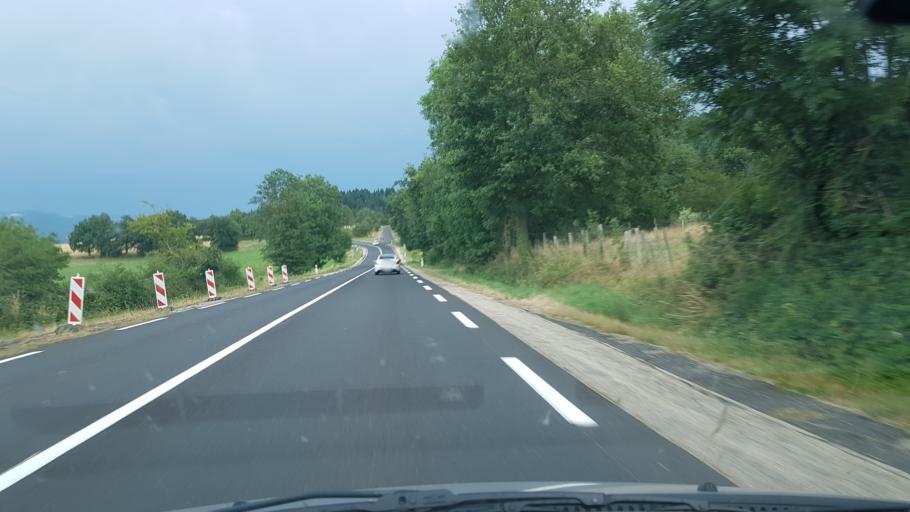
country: FR
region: Auvergne
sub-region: Departement de la Haute-Loire
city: Paulhaguet
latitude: 45.2288
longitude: 3.4752
